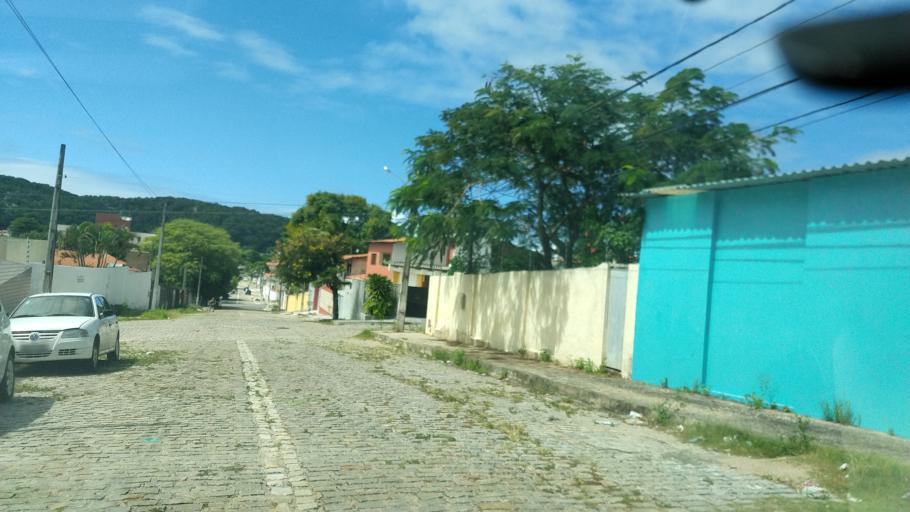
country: BR
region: Rio Grande do Norte
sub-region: Natal
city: Natal
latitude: -5.8208
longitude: -35.2032
